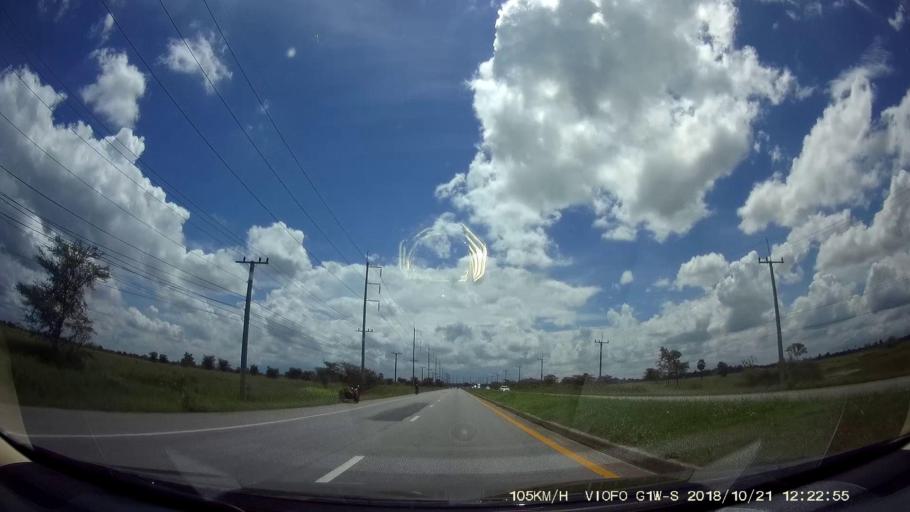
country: TH
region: Nakhon Ratchasima
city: Dan Khun Thot
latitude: 15.2537
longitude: 101.7891
